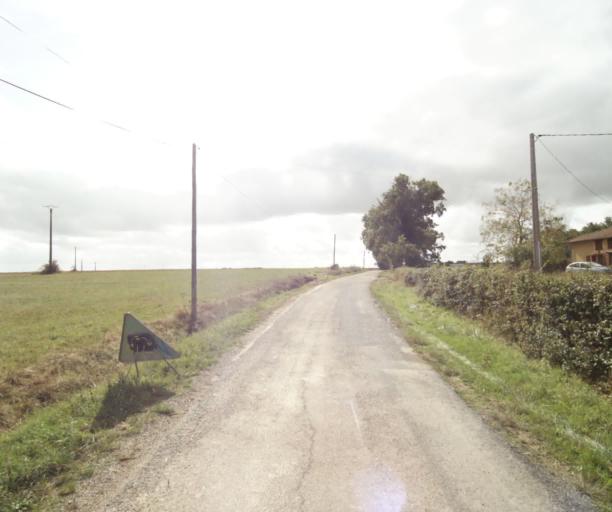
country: FR
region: Midi-Pyrenees
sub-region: Departement du Tarn-et-Garonne
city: Beaumont-de-Lomagne
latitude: 43.8668
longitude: 1.0679
